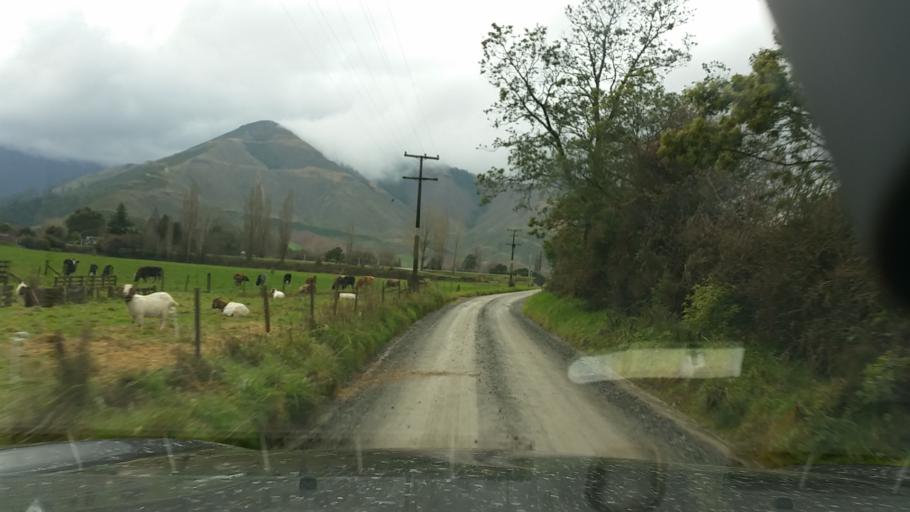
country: NZ
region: Marlborough
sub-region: Marlborough District
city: Picton
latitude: -41.2925
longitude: 173.6674
